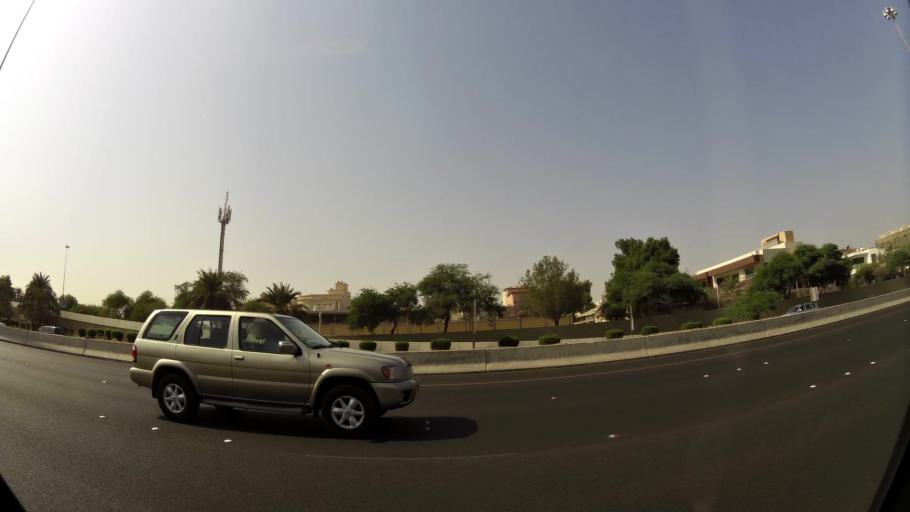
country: KW
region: Al Asimah
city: Ad Dasmah
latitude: 29.3516
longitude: 47.9933
